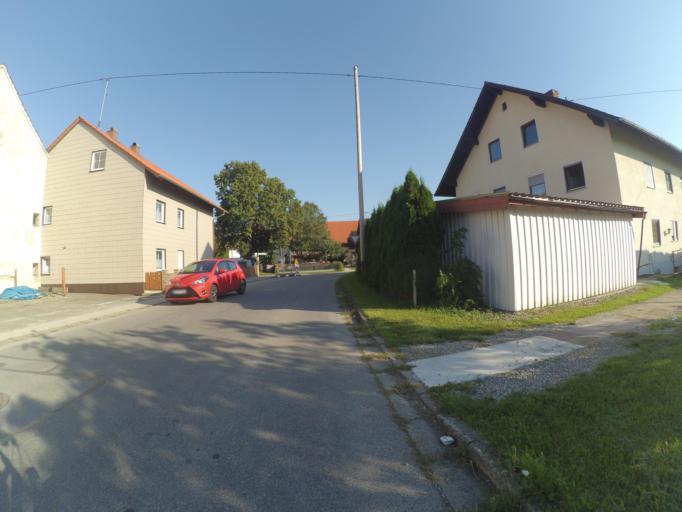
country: DE
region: Bavaria
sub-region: Swabia
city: Dirlewang
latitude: 48.0069
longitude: 10.5372
